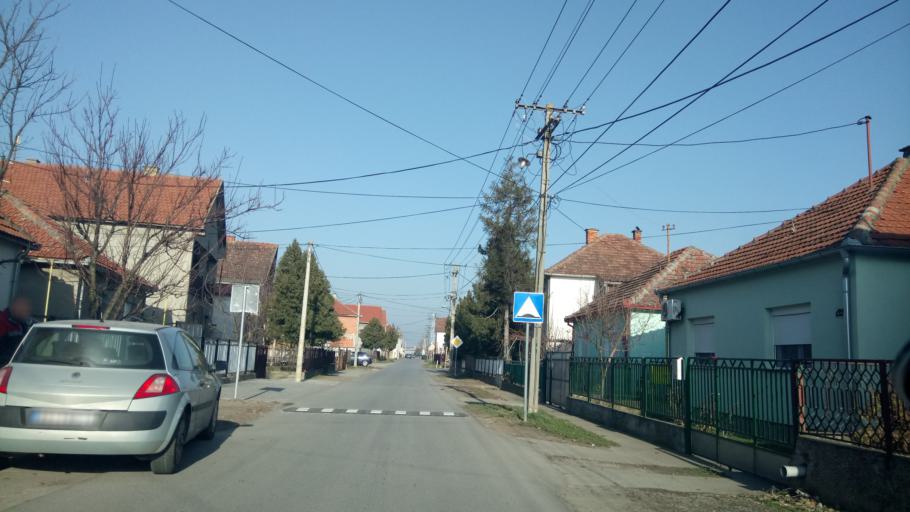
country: RS
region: Autonomna Pokrajina Vojvodina
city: Nova Pazova
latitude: 44.9454
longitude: 20.2047
